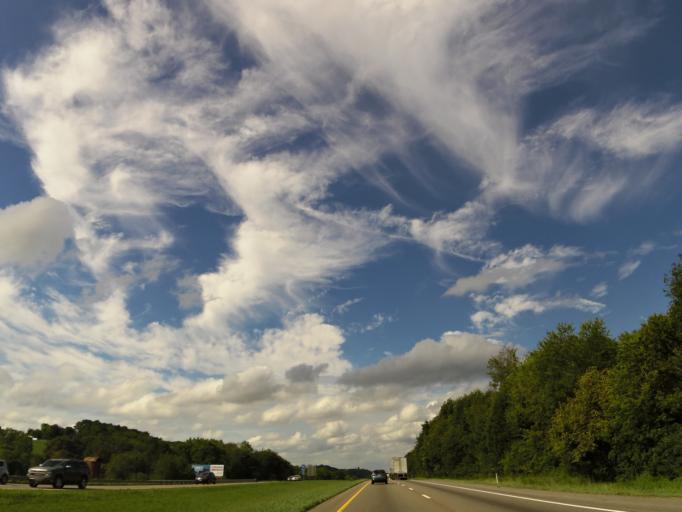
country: US
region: Tennessee
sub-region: Loudon County
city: Lenoir City
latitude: 35.8135
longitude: -84.2995
